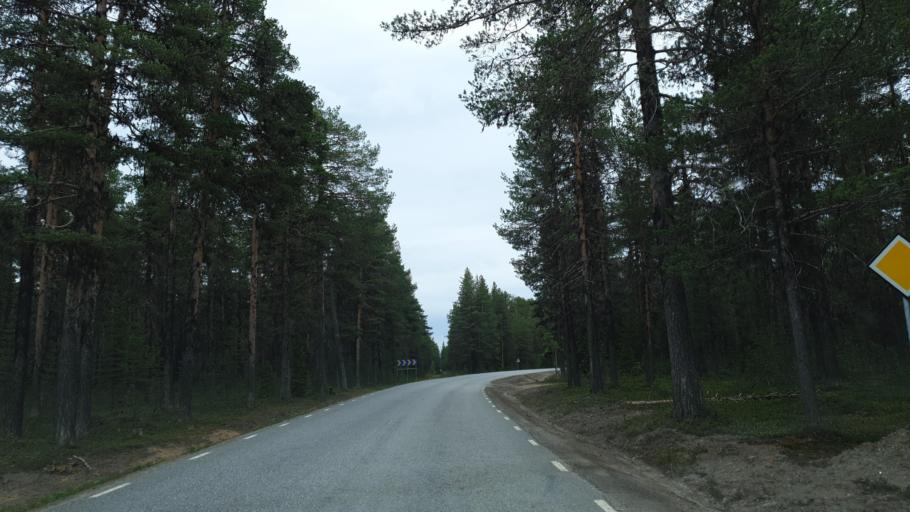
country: SE
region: Vaesterbotten
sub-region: Sorsele Kommun
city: Sorsele
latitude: 65.5515
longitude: 17.5083
